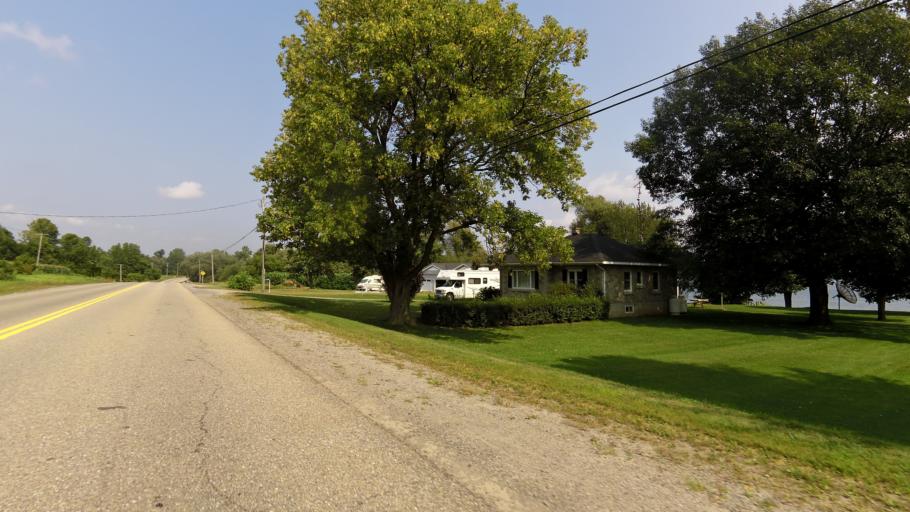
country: CA
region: Ontario
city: Prescott
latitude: 44.6721
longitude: -75.5672
